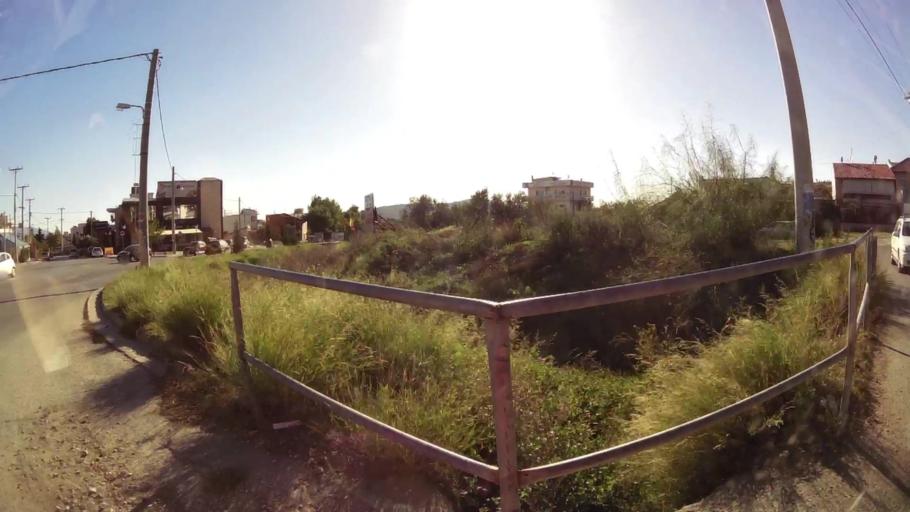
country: GR
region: Attica
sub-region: Nomarchia Anatolikis Attikis
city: Acharnes
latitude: 38.0952
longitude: 23.7244
